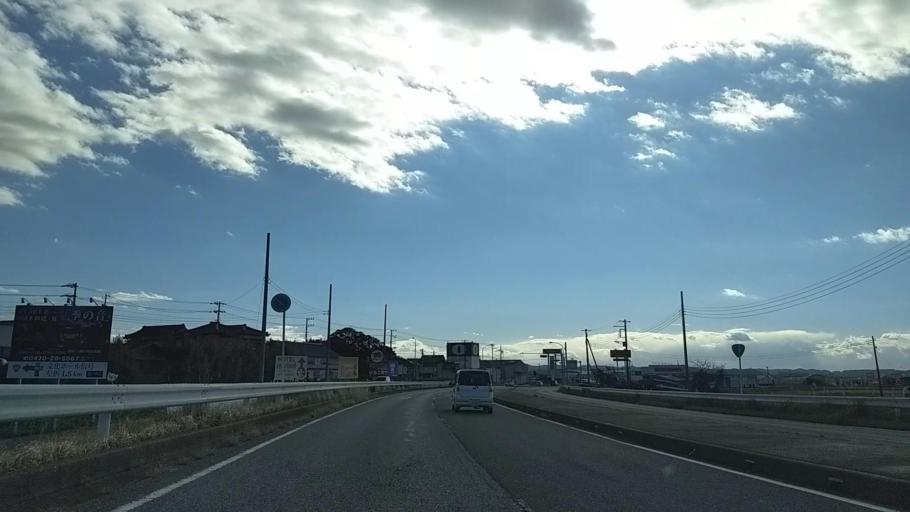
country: JP
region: Chiba
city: Tateyama
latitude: 35.0199
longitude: 139.8704
